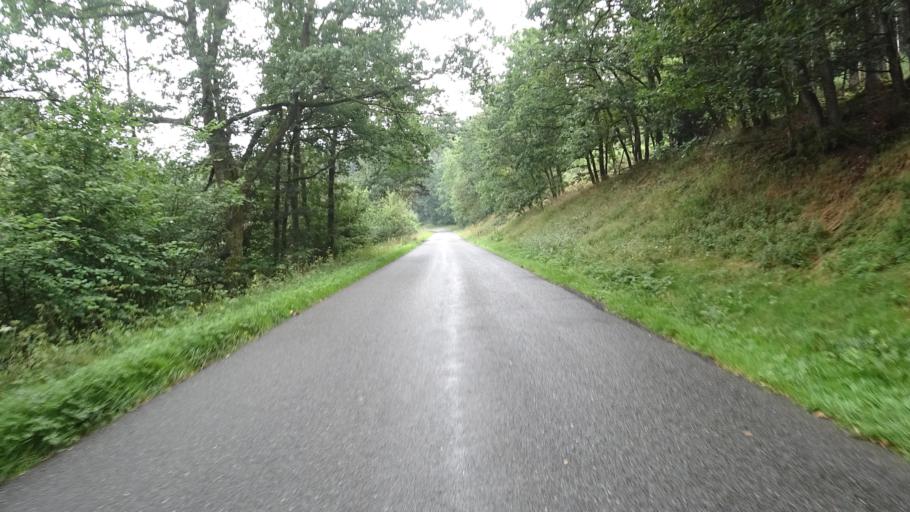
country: BE
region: Wallonia
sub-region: Province du Luxembourg
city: Chiny
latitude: 49.7888
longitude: 5.3747
